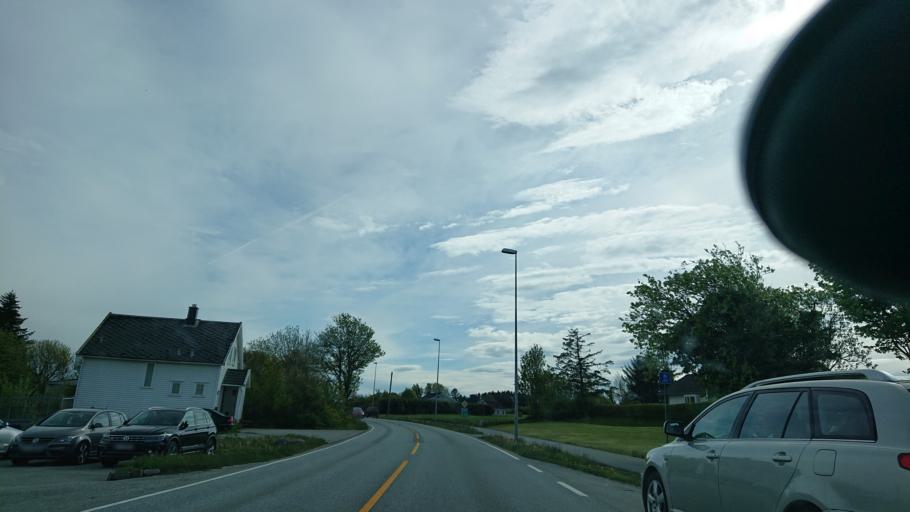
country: NO
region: Rogaland
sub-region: Sola
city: Tananger
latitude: 58.9498
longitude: 5.6016
